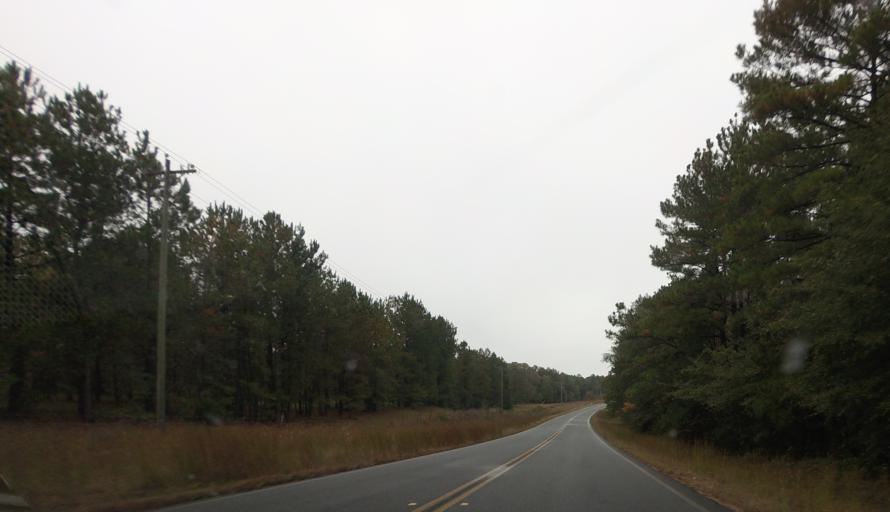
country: US
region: Georgia
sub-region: Marion County
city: Buena Vista
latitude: 32.3892
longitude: -84.4302
